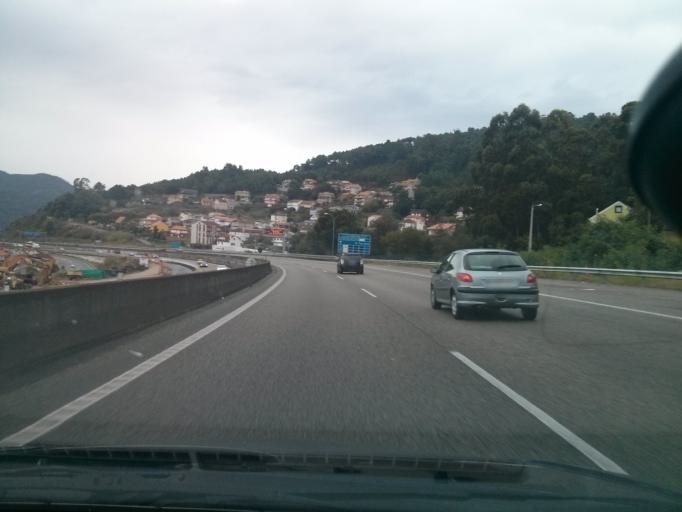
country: ES
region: Galicia
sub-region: Provincia de Pontevedra
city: Redondela
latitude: 42.2686
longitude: -8.6640
